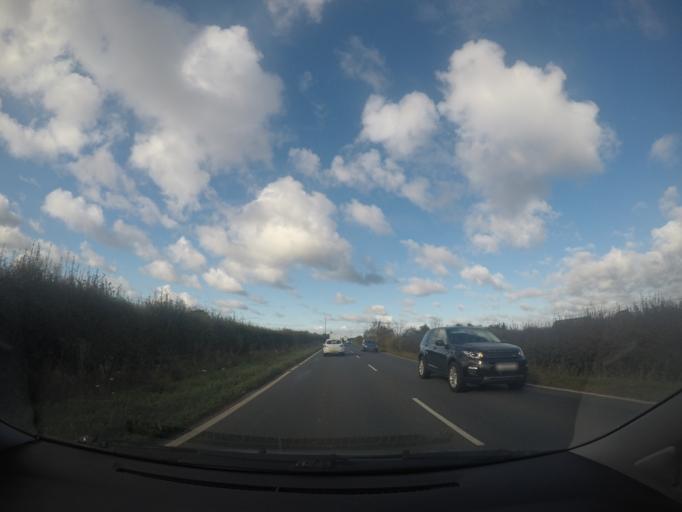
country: GB
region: England
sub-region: City of York
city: Askham Richard
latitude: 53.9890
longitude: -1.2289
